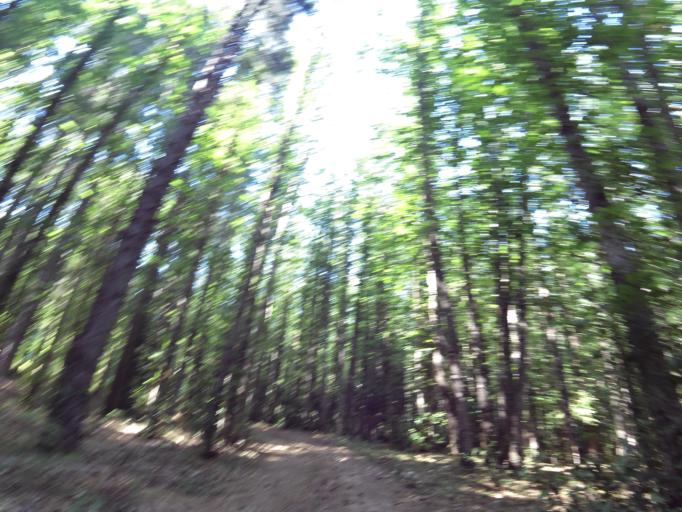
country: IT
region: Calabria
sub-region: Provincia di Vibo-Valentia
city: Nardodipace
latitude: 38.4971
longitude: 16.3850
